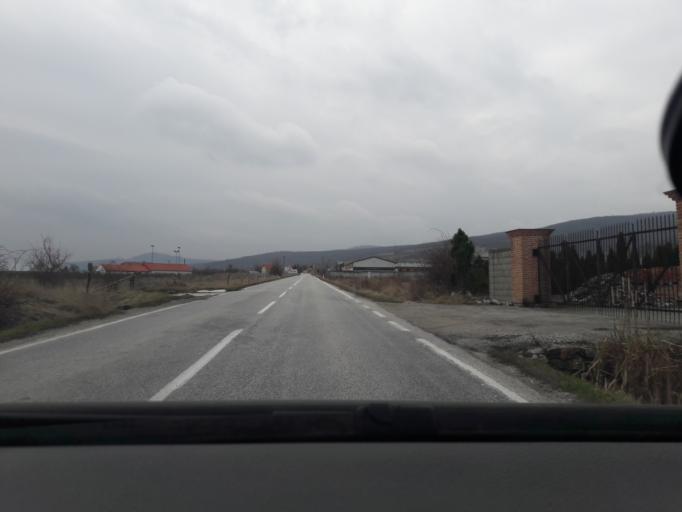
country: SK
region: Trnavsky
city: Smolenice
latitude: 48.4184
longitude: 17.3866
